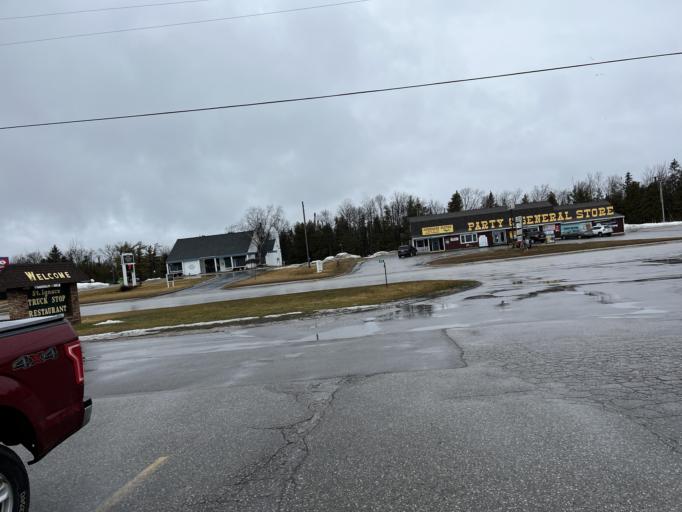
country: US
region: Michigan
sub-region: Mackinac County
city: Saint Ignace
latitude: 45.8562
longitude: -84.7362
